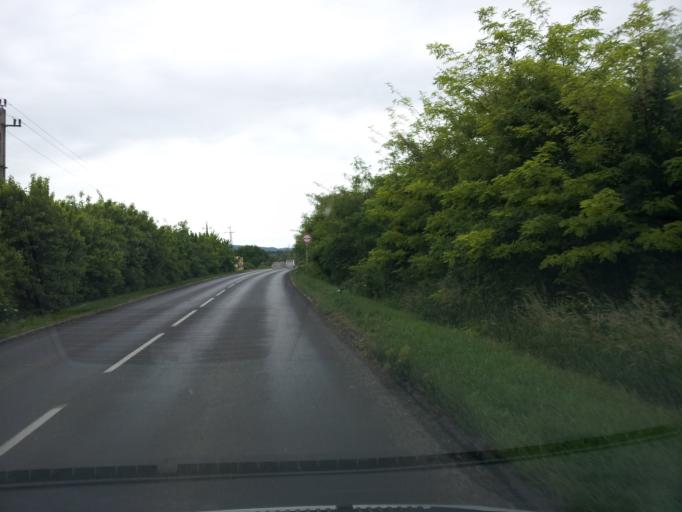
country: HU
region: Pest
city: Csobanka
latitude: 47.6552
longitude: 18.9797
